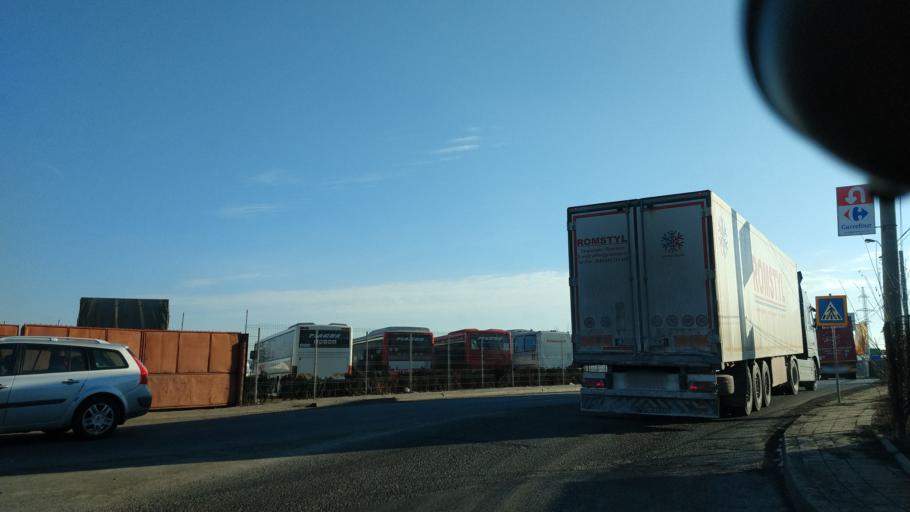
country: RO
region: Neamt
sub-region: Municipiul Roman
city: Roman
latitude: 46.9266
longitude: 26.9087
